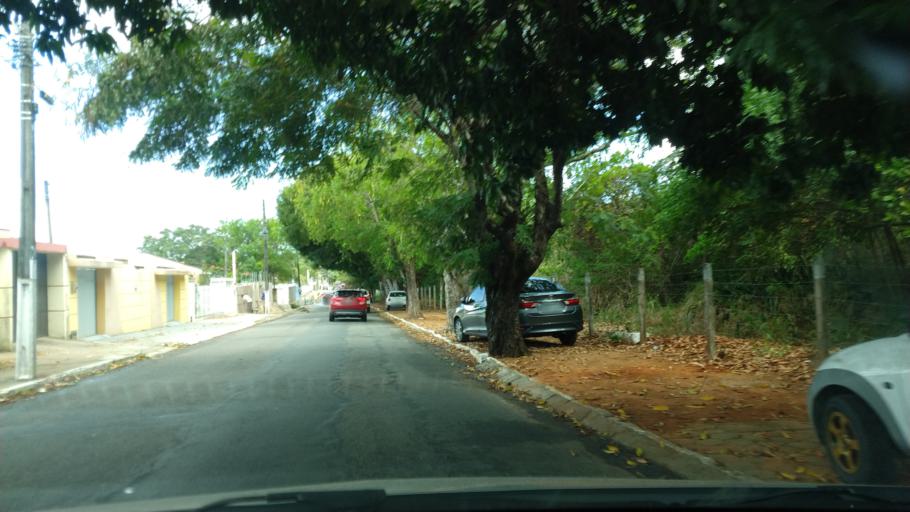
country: BR
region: Rio Grande do Norte
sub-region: Natal
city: Natal
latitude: -5.8499
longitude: -35.1983
